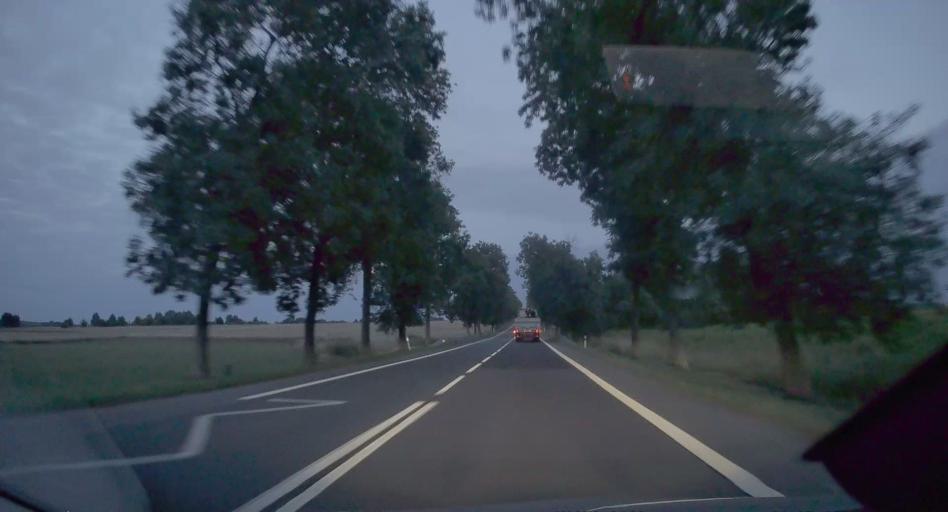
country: PL
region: Silesian Voivodeship
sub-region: Powiat klobucki
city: Klobuck
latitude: 50.9197
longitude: 18.8833
